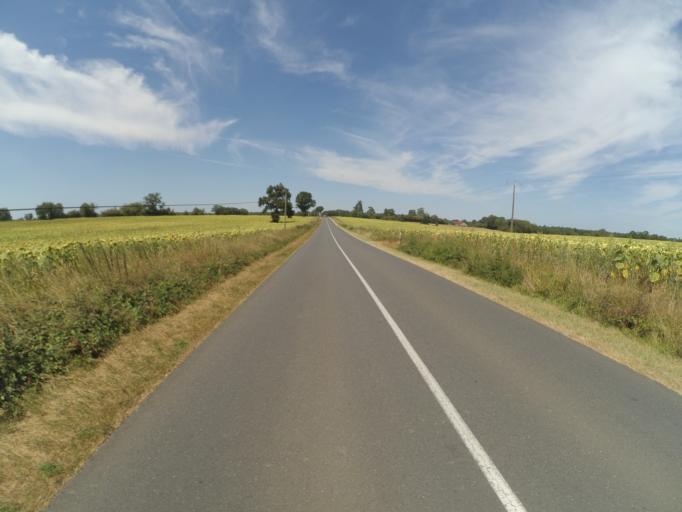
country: FR
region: Poitou-Charentes
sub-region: Departement de la Vienne
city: Usson-du-Poitou
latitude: 46.2051
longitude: 0.5340
